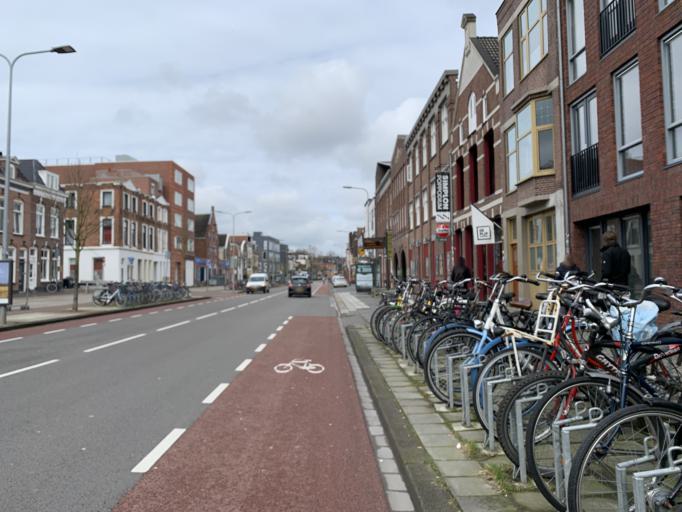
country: NL
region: Groningen
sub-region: Gemeente Groningen
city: Groningen
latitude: 53.2243
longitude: 6.5642
